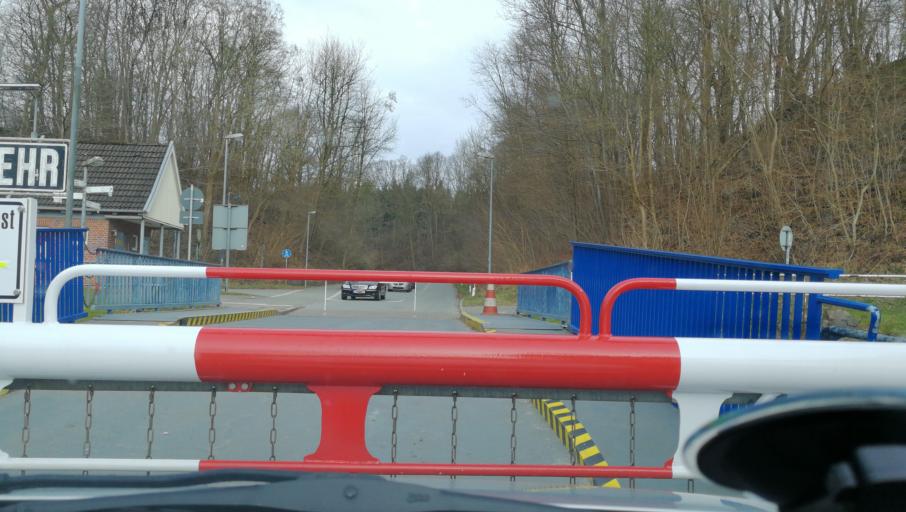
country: DE
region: Schleswig-Holstein
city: Quarnbek
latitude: 54.3459
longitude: 9.9850
